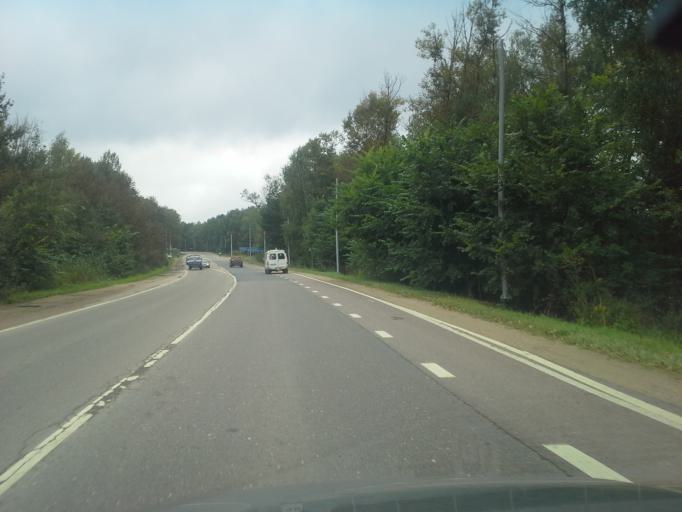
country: RU
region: Moskovskaya
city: Chupryakovo
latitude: 55.5734
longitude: 36.6412
